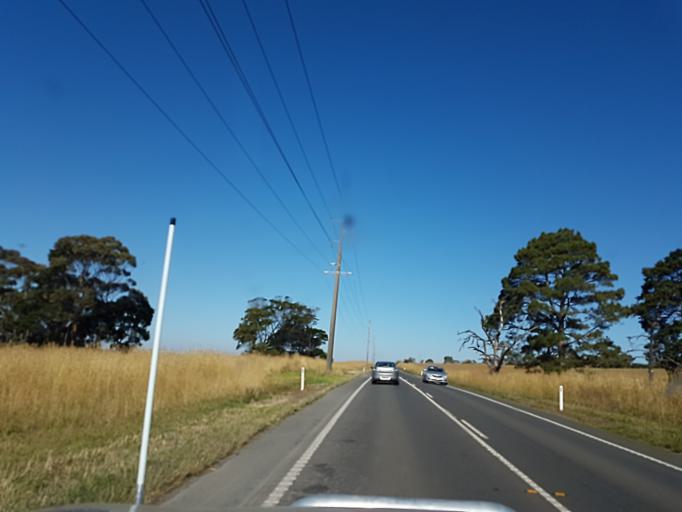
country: AU
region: Victoria
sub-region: Colac-Otway
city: Colac
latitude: -38.3120
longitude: 143.6905
